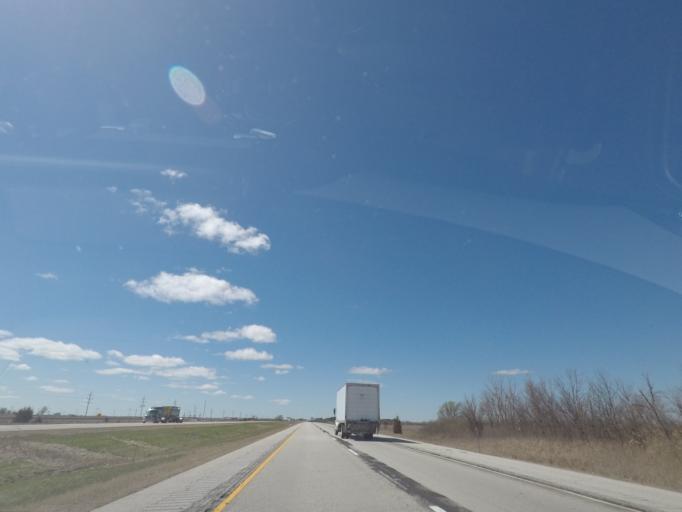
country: US
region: Illinois
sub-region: Livingston County
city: Dwight
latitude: 41.0612
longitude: -88.4686
